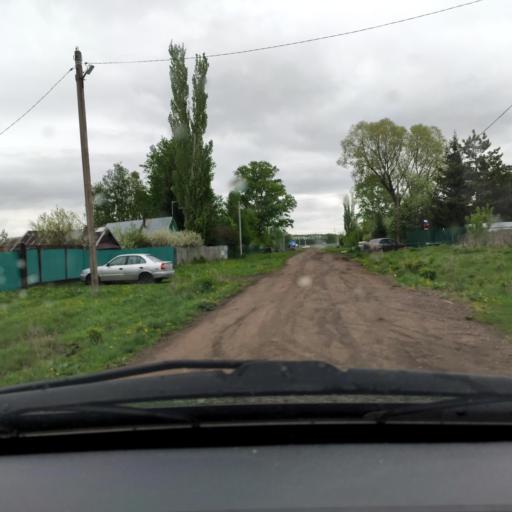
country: RU
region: Bashkortostan
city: Asanovo
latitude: 55.0003
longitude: 55.4933
